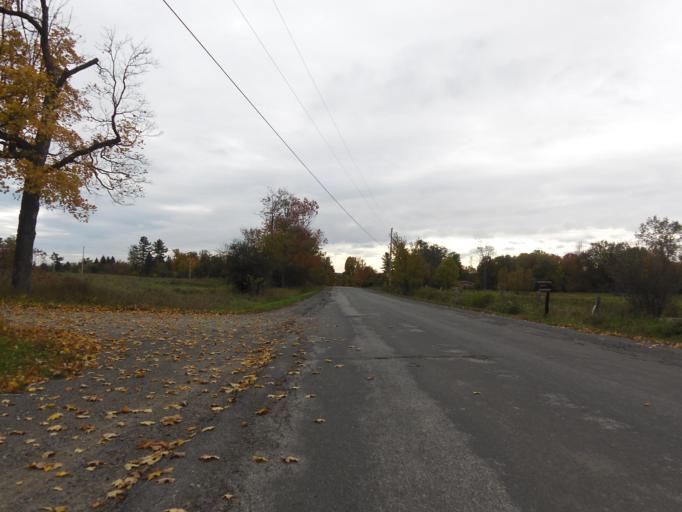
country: CA
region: Ontario
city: Arnprior
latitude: 45.4651
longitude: -76.1491
